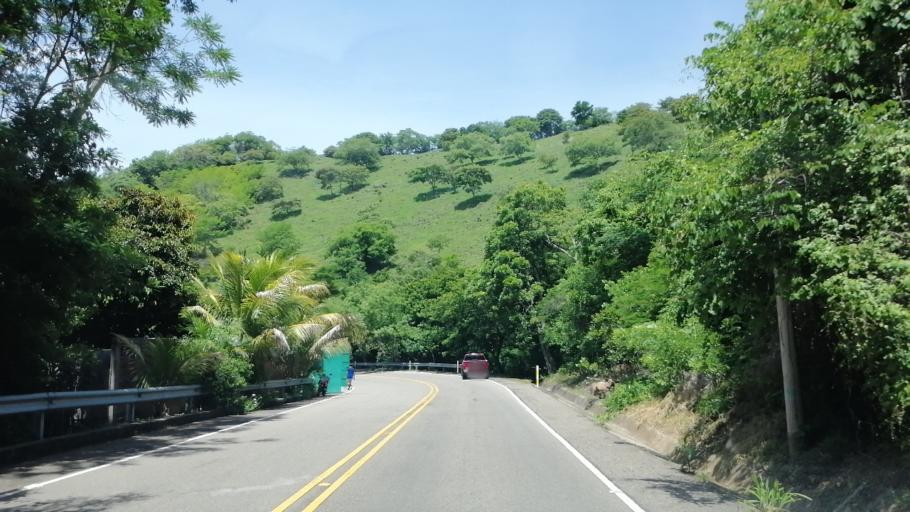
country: SV
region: Chalatenango
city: Nueva Concepcion
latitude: 14.1704
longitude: -89.3112
